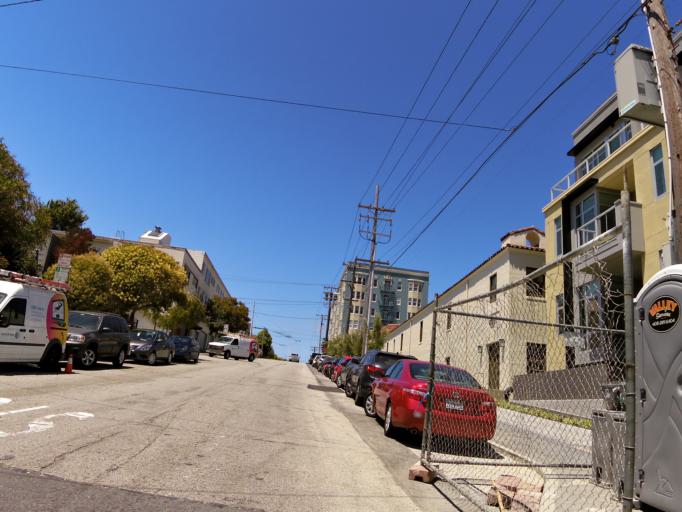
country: US
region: California
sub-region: San Francisco County
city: San Francisco
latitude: 37.7717
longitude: -122.4270
